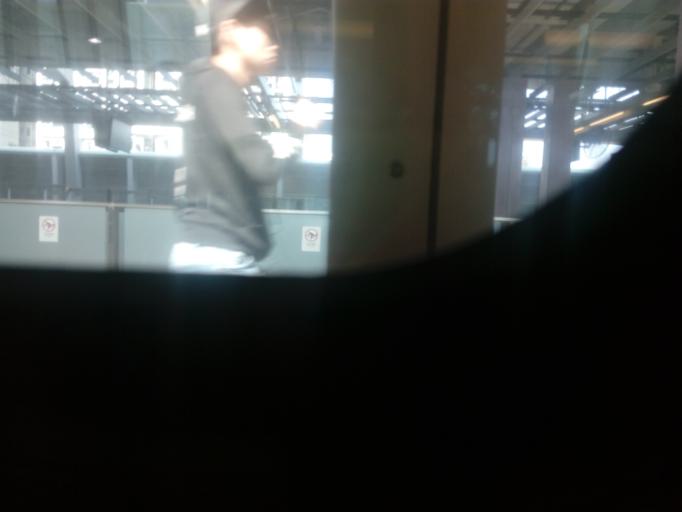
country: HK
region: Sai Kung
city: Sai Kung
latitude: 22.4246
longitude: 114.2314
